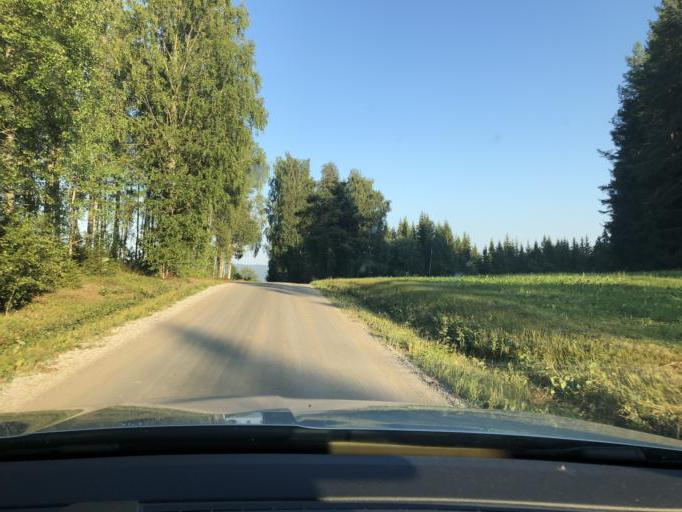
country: SE
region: Vaesternorrland
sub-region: Kramfors Kommun
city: Bollstabruk
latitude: 63.0522
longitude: 17.7154
